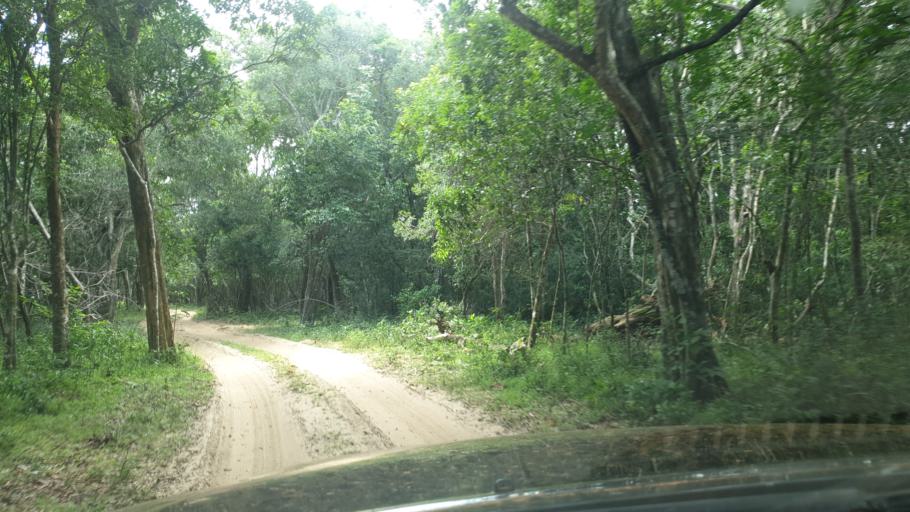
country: LK
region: North Western
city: Puttalam
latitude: 8.4144
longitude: 79.9942
